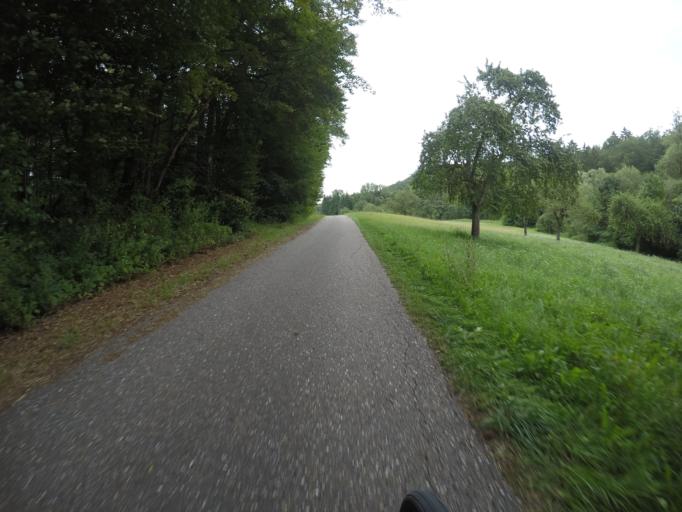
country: DE
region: Baden-Wuerttemberg
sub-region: Regierungsbezirk Stuttgart
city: Nufringen
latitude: 48.6156
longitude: 8.9113
